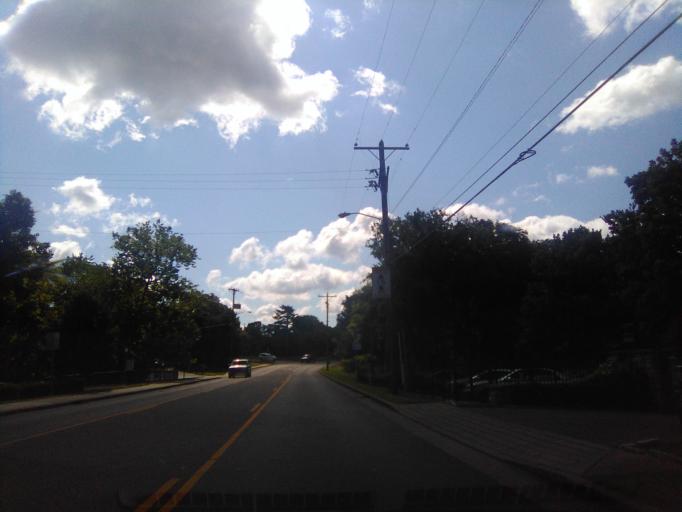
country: US
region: Tennessee
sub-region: Davidson County
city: Belle Meade
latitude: 36.1016
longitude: -86.8686
